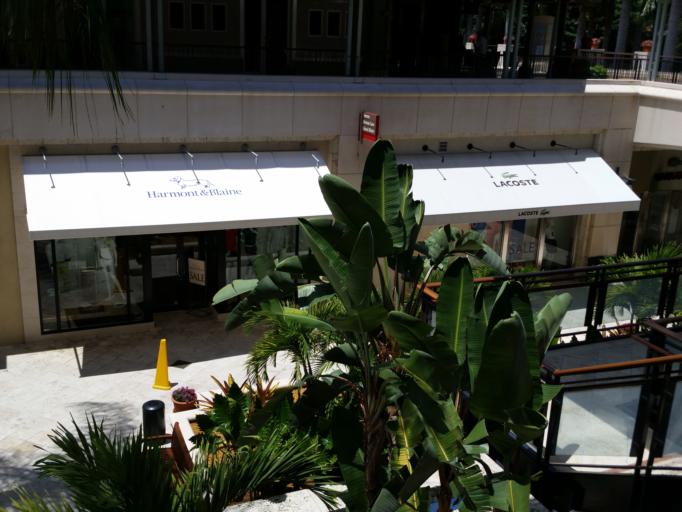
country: US
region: Florida
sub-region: Miami-Dade County
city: Coral Gables
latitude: 25.7317
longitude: -80.2608
